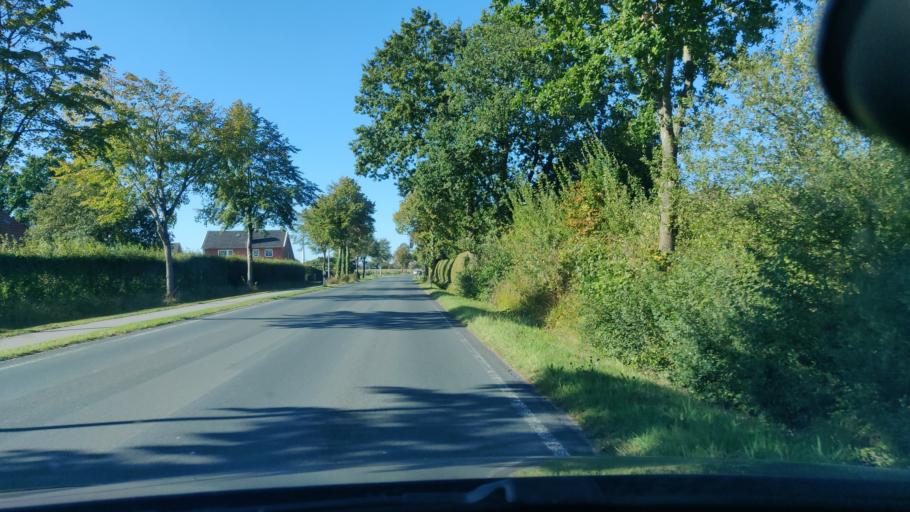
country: DE
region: Lower Saxony
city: Aurich
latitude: 53.4819
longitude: 7.4492
